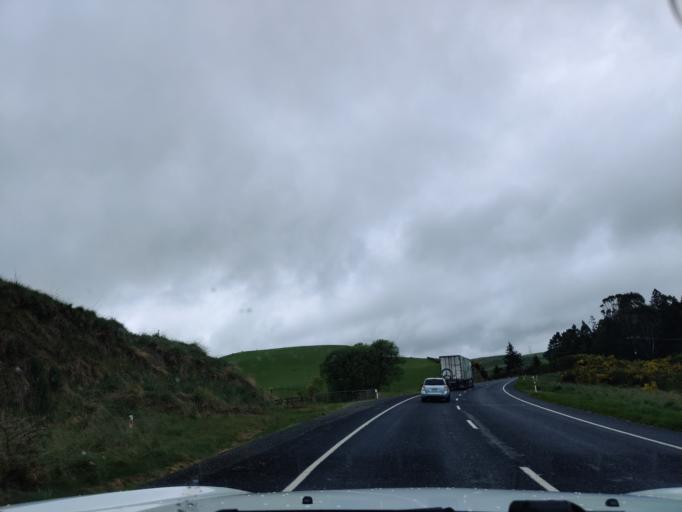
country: NZ
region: Manawatu-Wanganui
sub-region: Ruapehu District
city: Waiouru
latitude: -39.5496
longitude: 175.6858
